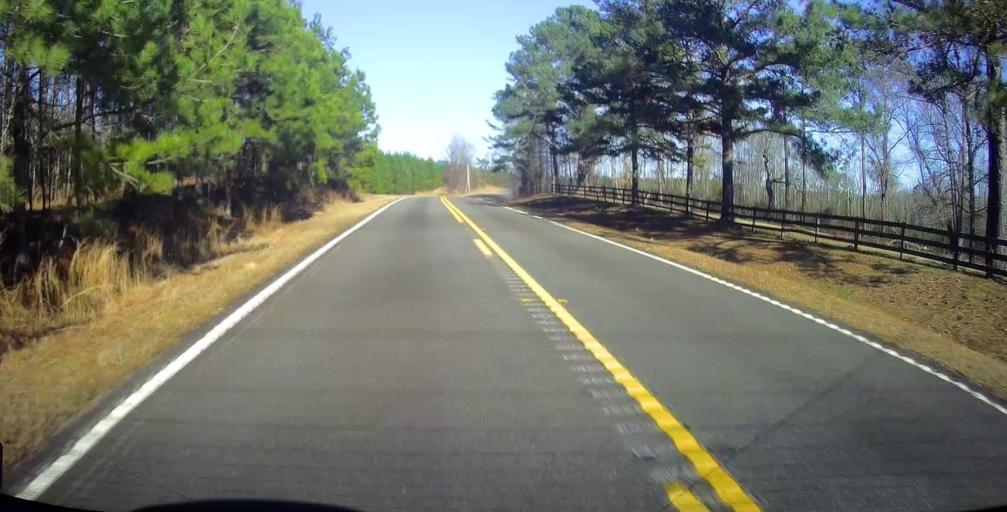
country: US
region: Georgia
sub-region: Talbot County
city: Talbotton
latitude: 32.6495
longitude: -84.3957
